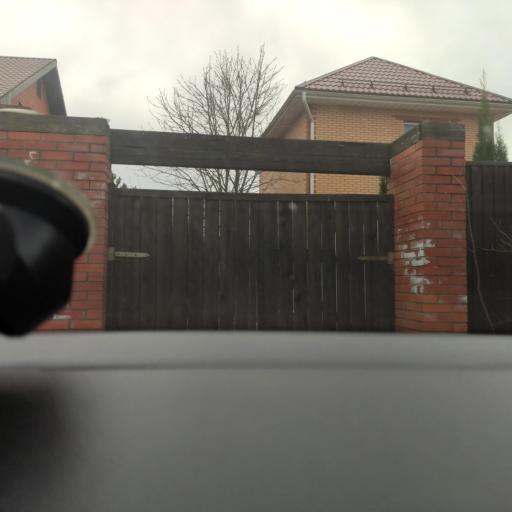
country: RU
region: Moskovskaya
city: Zvenigorod
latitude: 55.7452
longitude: 36.8681
